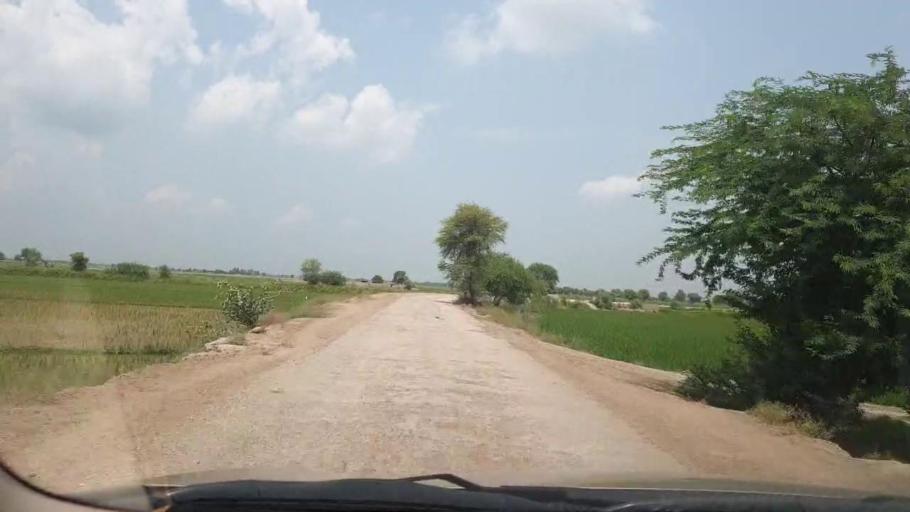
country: PK
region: Sindh
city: Larkana
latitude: 27.6075
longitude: 68.1440
